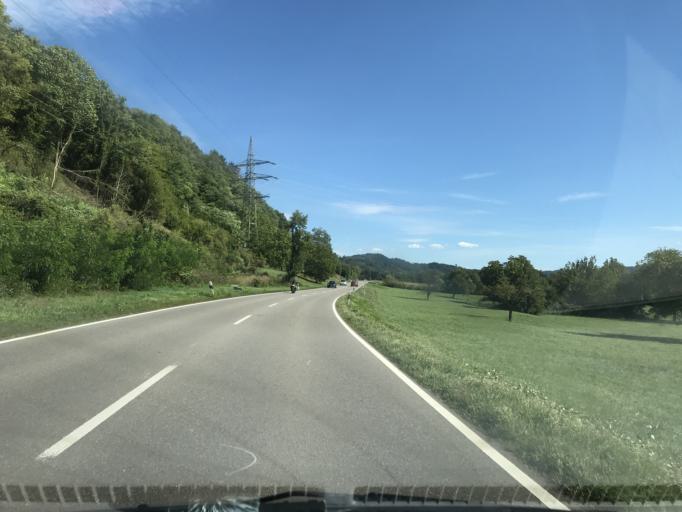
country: DE
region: Baden-Wuerttemberg
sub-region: Freiburg Region
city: Schworstadt
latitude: 47.5913
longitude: 7.8912
